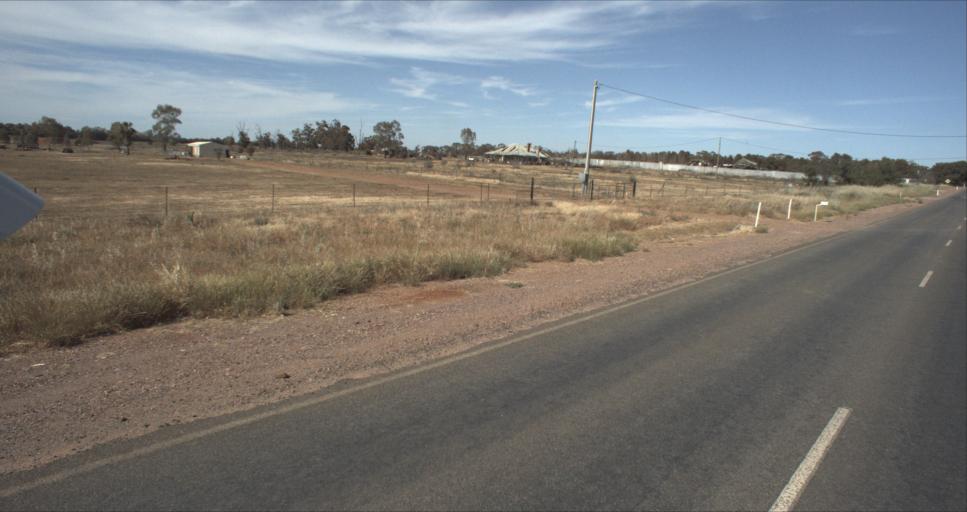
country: AU
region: New South Wales
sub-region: Leeton
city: Leeton
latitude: -34.5636
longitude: 146.4288
